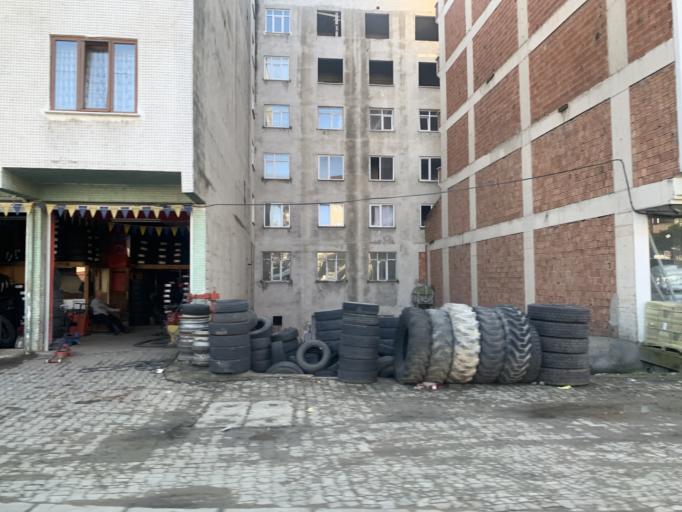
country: TR
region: Trabzon
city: Of
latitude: 40.9426
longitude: 40.2666
